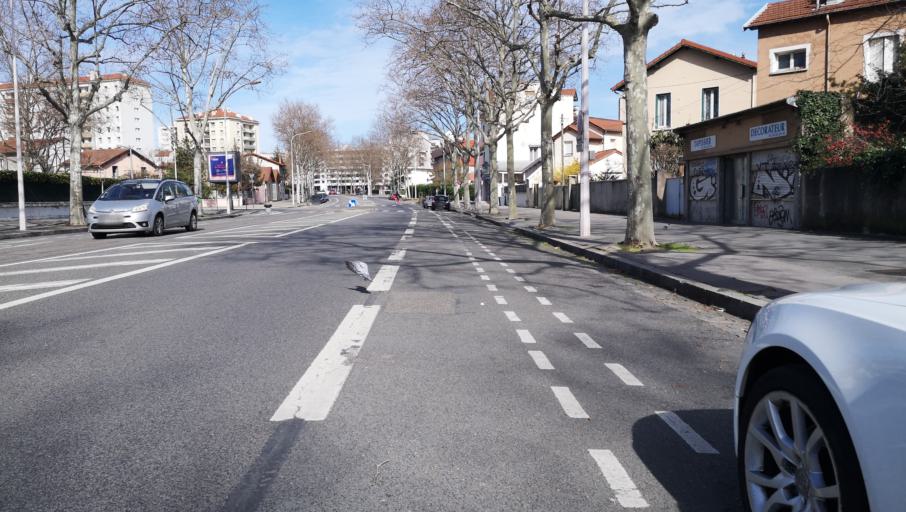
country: FR
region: Rhone-Alpes
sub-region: Departement du Rhone
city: Villeurbanne
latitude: 45.7353
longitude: 4.8826
